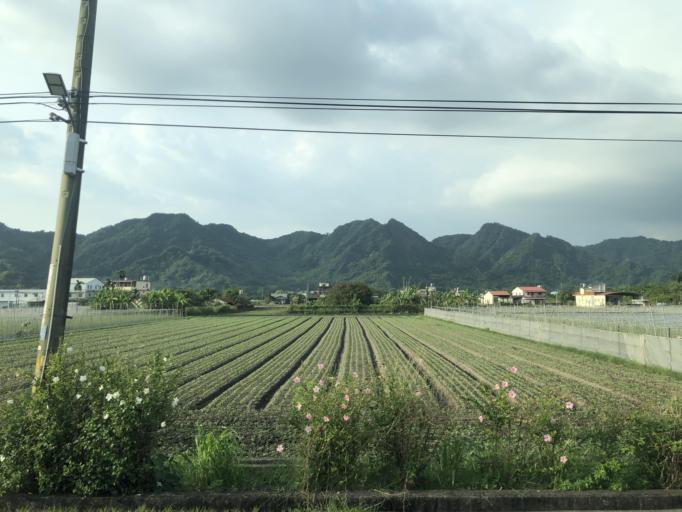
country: TW
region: Taiwan
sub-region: Pingtung
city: Pingtung
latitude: 22.8857
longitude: 120.5115
